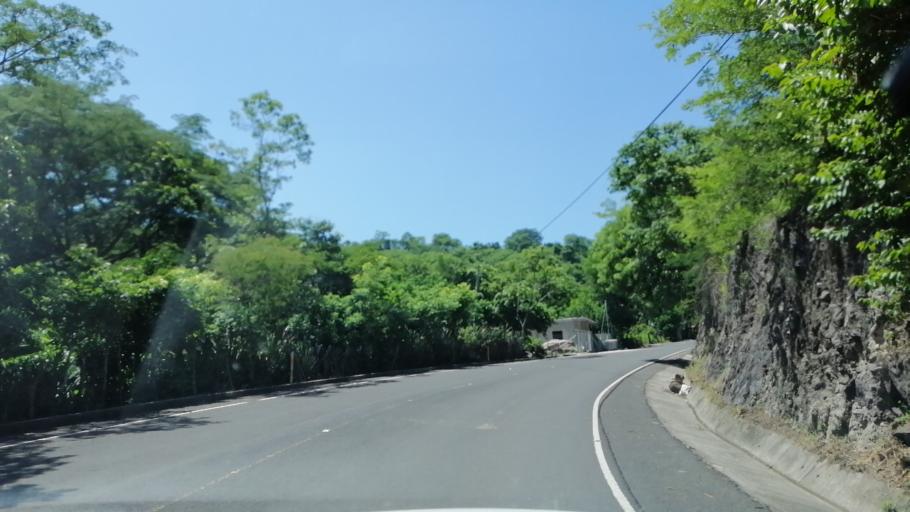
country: SV
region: San Miguel
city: Sesori
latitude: 13.8112
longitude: -88.4030
